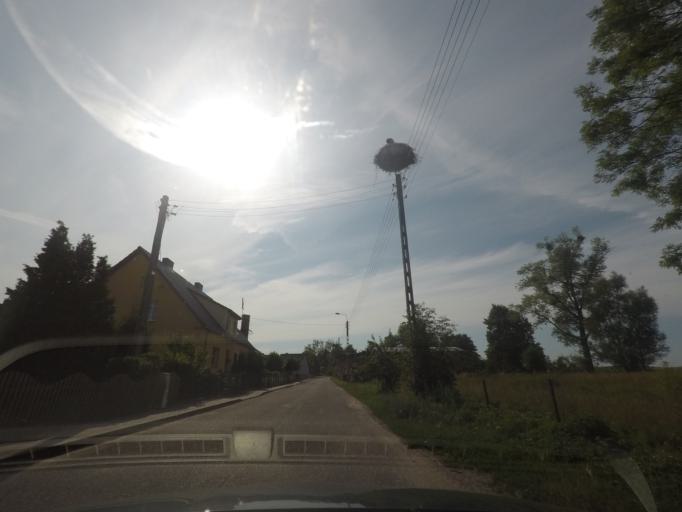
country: PL
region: Pomeranian Voivodeship
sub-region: Powiat slupski
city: Smoldzino
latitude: 54.6314
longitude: 17.2584
